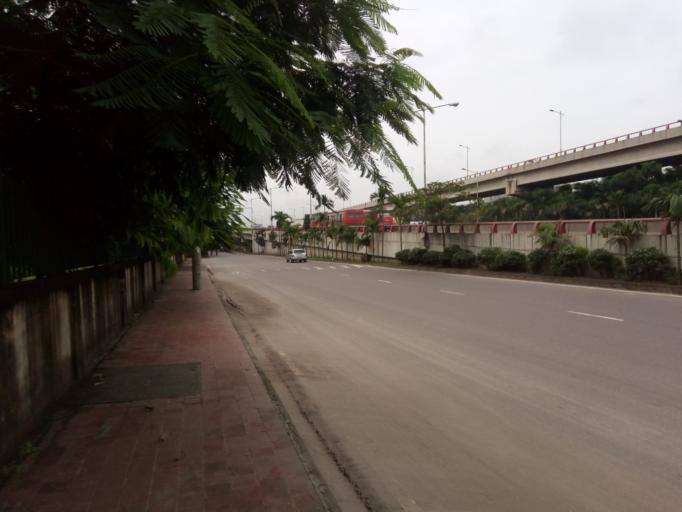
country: BD
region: Dhaka
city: Tungi
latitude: 23.8141
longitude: 90.4045
